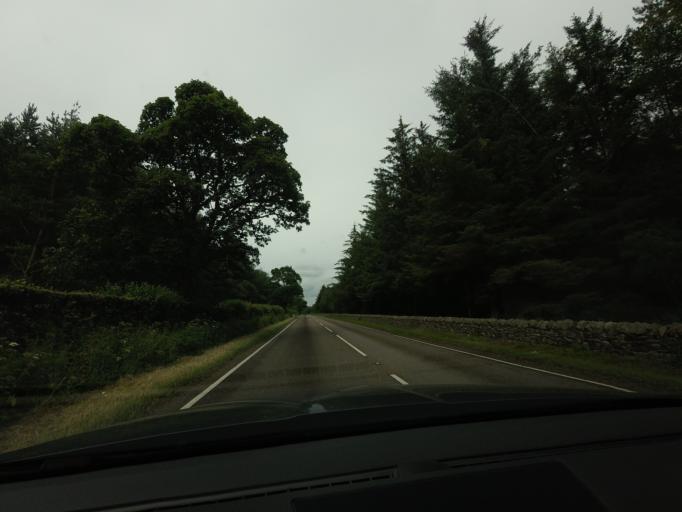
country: GB
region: Scotland
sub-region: Moray
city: Findochty
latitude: 57.6815
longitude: -2.8904
